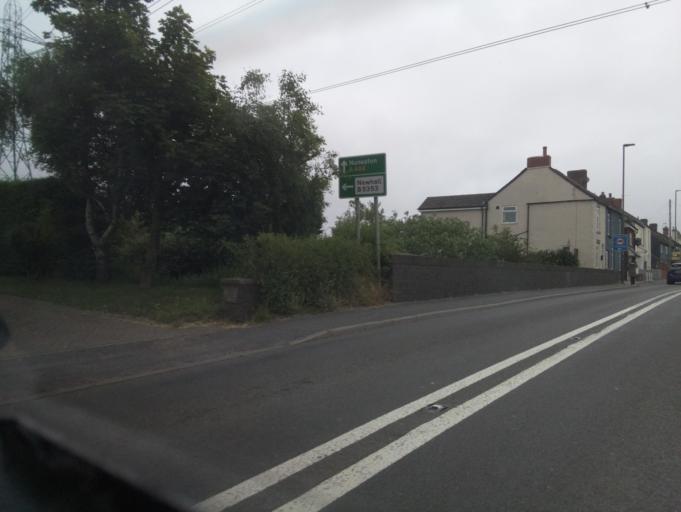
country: GB
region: England
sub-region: Derbyshire
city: Swadlincote
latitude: 52.7762
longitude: -1.6024
